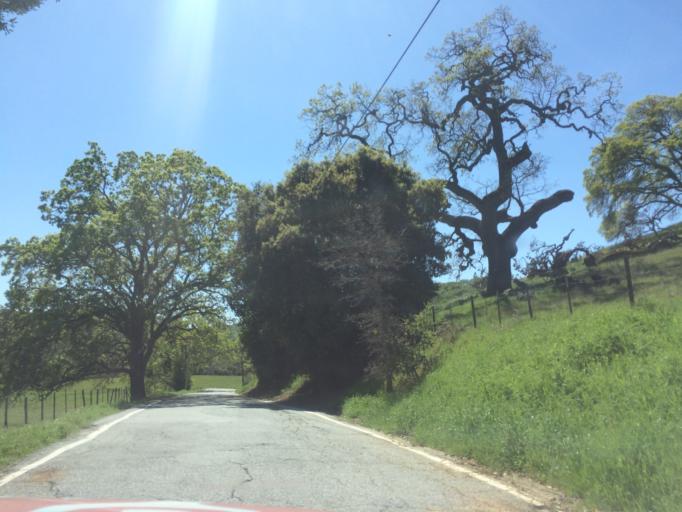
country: US
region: California
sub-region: Santa Clara County
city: Morgan Hill
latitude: 37.1735
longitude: -121.5688
